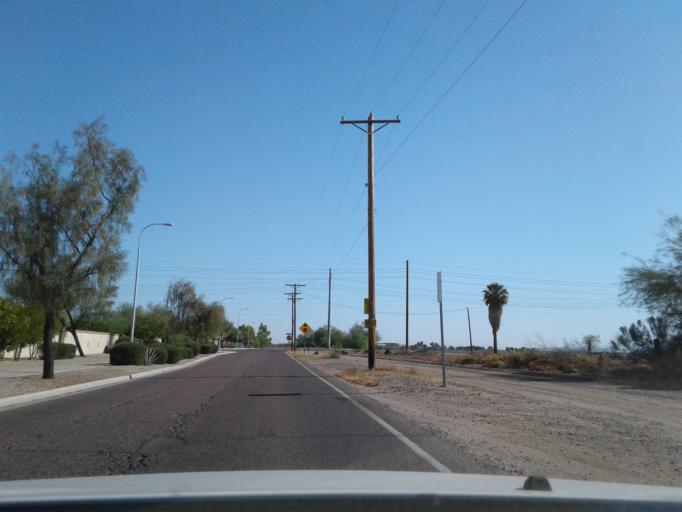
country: US
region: Arizona
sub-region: Maricopa County
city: Laveen
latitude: 33.4216
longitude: -112.1953
